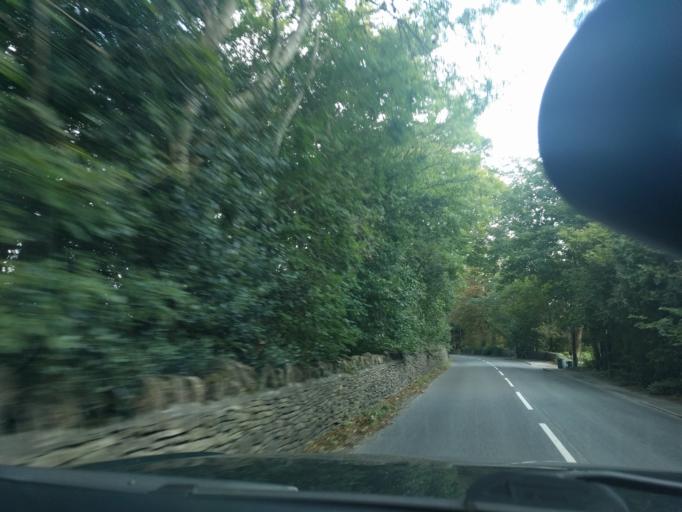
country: GB
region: England
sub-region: Bath and North East Somerset
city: Freshford
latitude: 51.3679
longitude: -2.3181
